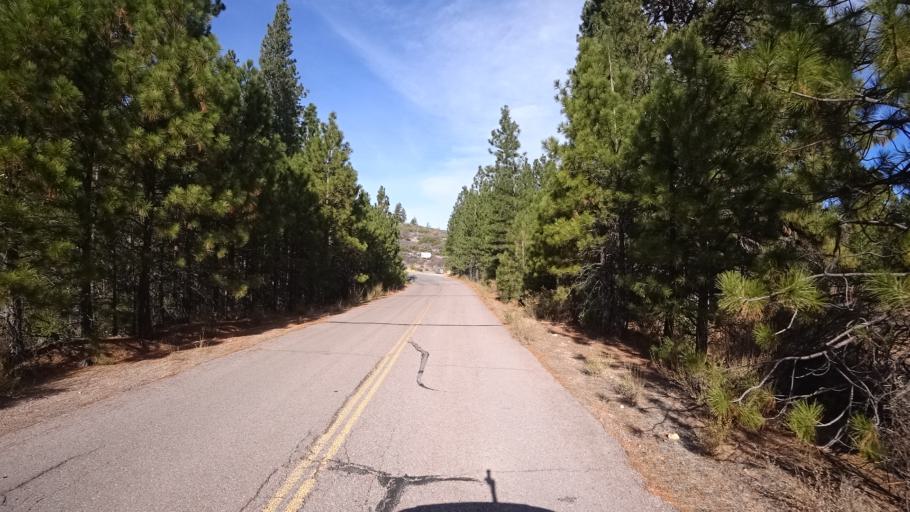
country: US
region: California
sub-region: Siskiyou County
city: Weed
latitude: 41.4242
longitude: -122.3992
